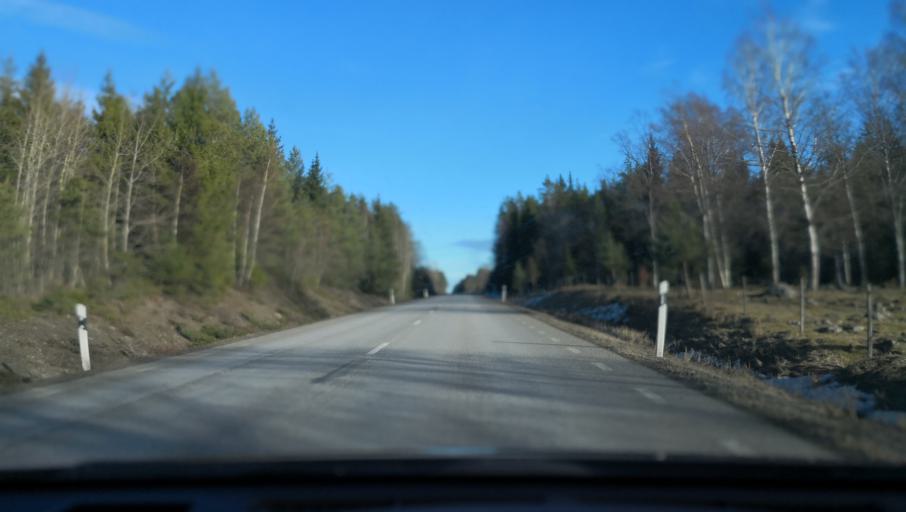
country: SE
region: Uppsala
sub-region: Osthammars Kommun
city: Osterbybruk
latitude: 60.1615
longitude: 18.0121
